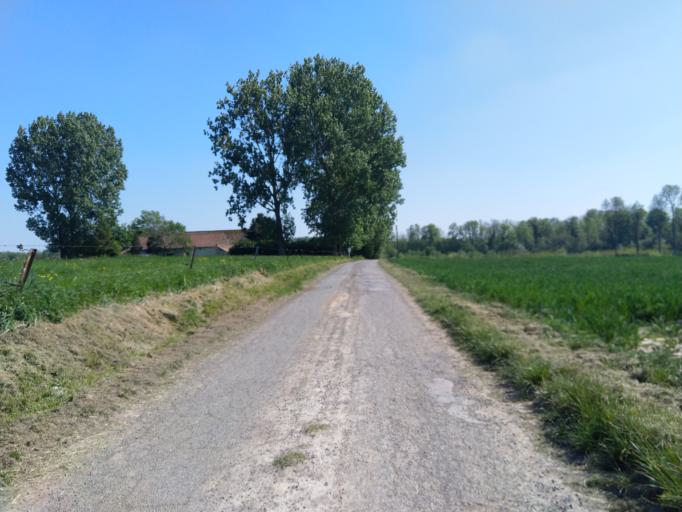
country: BE
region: Wallonia
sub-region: Province du Hainaut
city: Jurbise
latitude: 50.5395
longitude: 3.9869
